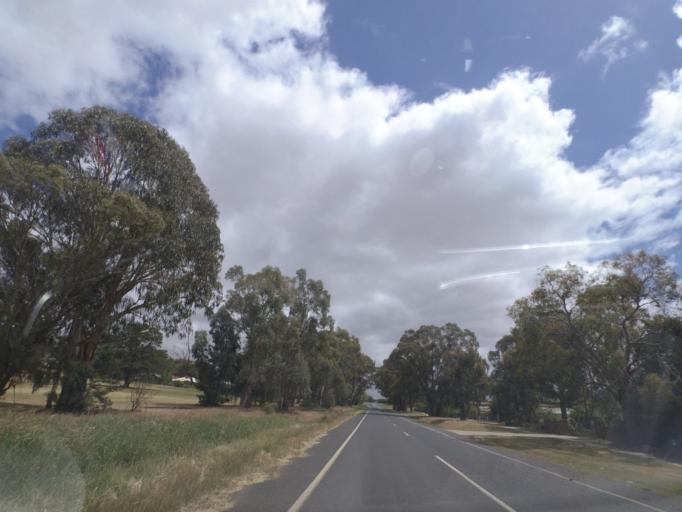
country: AU
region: Victoria
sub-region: Whittlesea
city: Whittlesea
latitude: -37.2123
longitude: 145.0482
